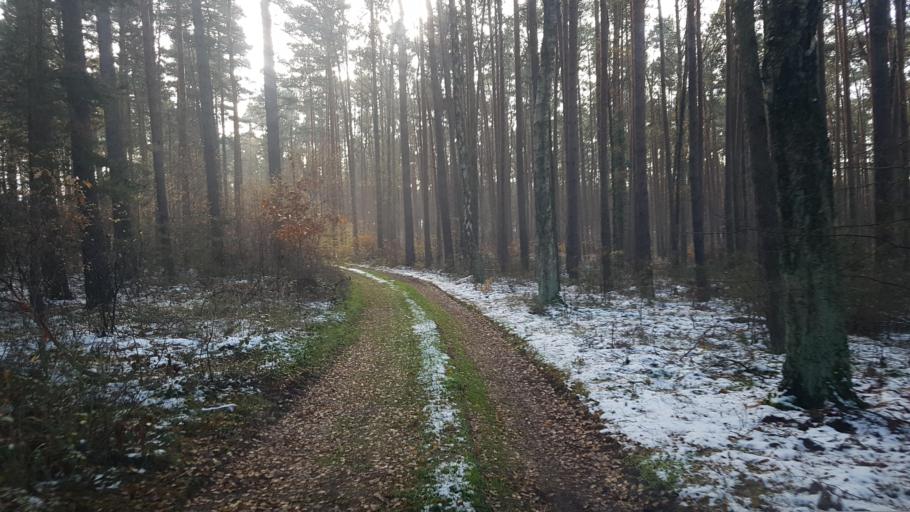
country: DE
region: Brandenburg
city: Bronkow
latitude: 51.6616
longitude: 13.8976
